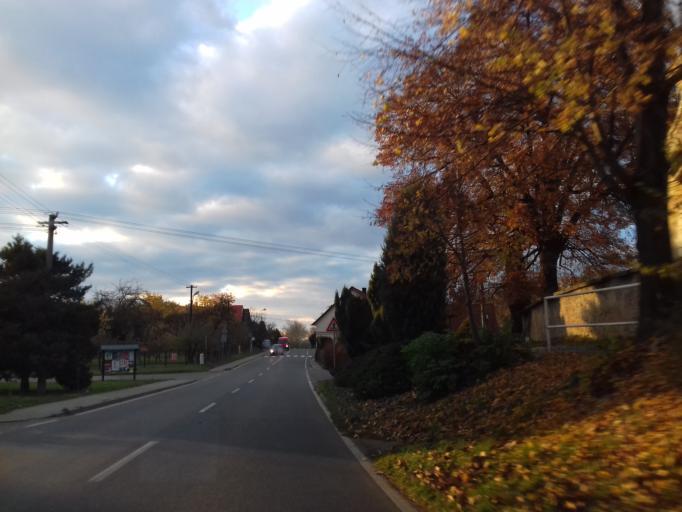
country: CZ
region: Pardubicky
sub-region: Okres Chrudim
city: Skutec
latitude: 49.8363
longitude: 16.0187
